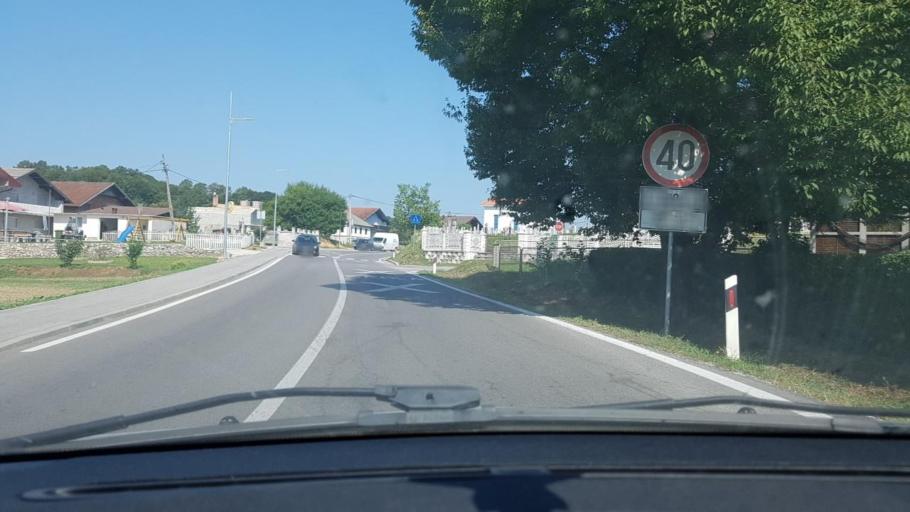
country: BA
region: Federation of Bosnia and Herzegovina
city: Mala Kladusa
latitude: 45.1411
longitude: 15.8452
